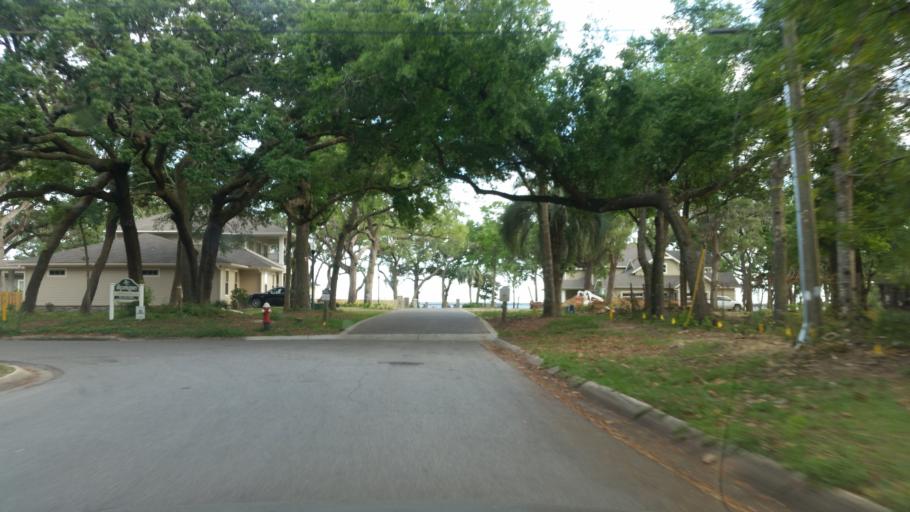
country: US
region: Florida
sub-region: Escambia County
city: East Pensacola Heights
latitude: 30.4227
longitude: -87.1854
